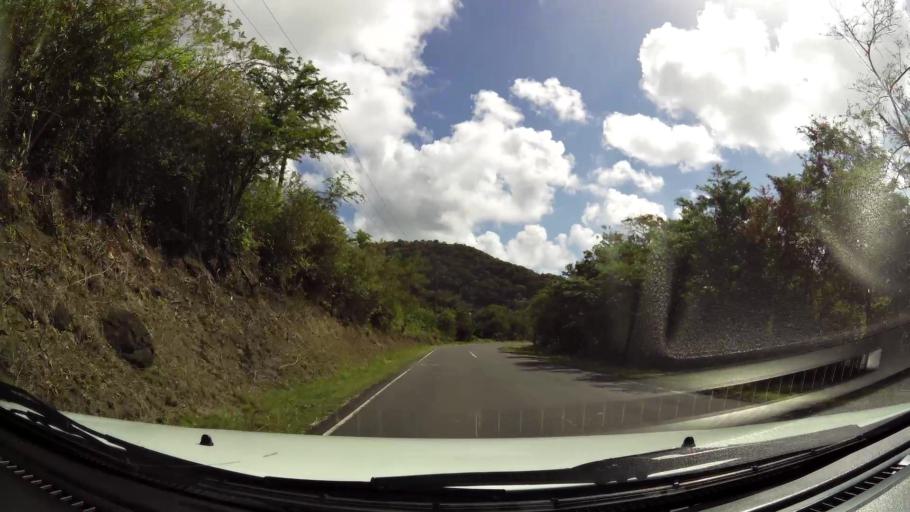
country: LC
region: Laborie Quarter
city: Laborie
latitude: 13.7553
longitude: -61.0104
